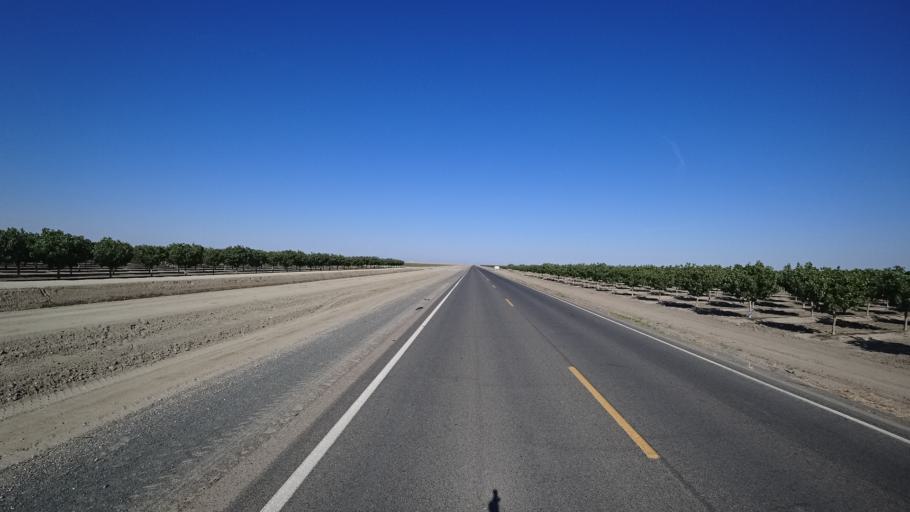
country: US
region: California
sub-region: Kings County
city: Corcoran
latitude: 36.0980
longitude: -119.5971
